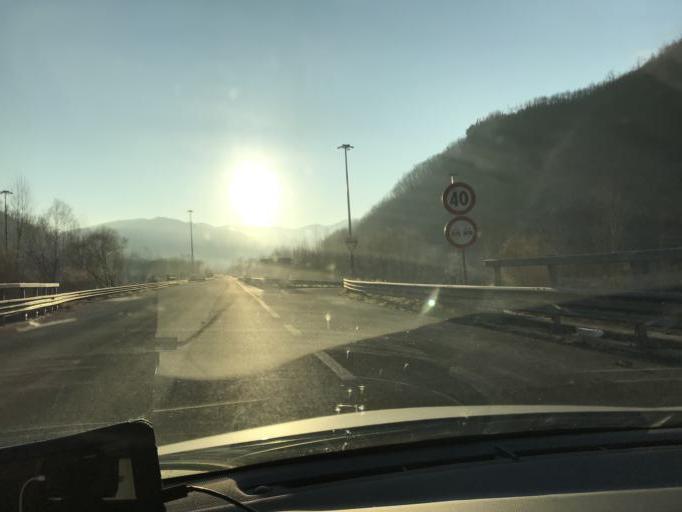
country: IT
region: Latium
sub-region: Provincia di Rieti
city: Concerviano
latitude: 42.3348
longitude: 12.9755
